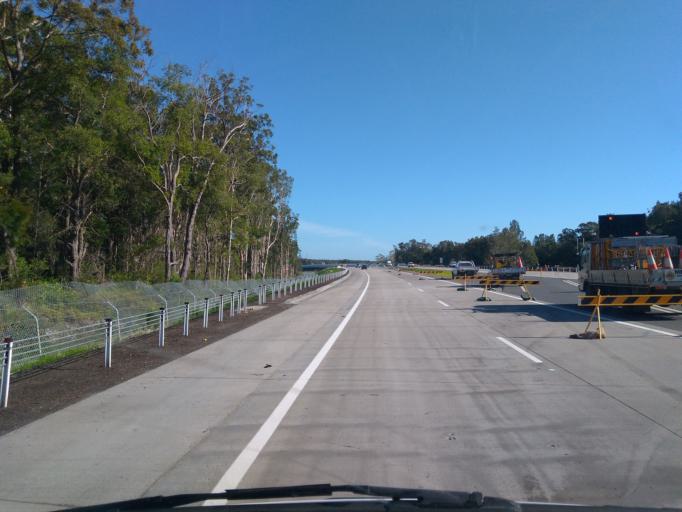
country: AU
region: New South Wales
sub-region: Port Macquarie-Hastings
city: North Shore
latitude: -31.4240
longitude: 152.8235
